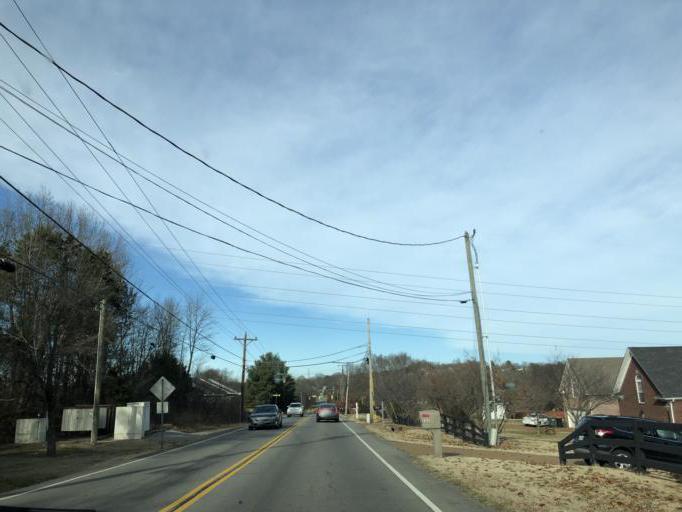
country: US
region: Tennessee
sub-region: Wilson County
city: Green Hill
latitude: 36.1589
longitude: -86.5857
